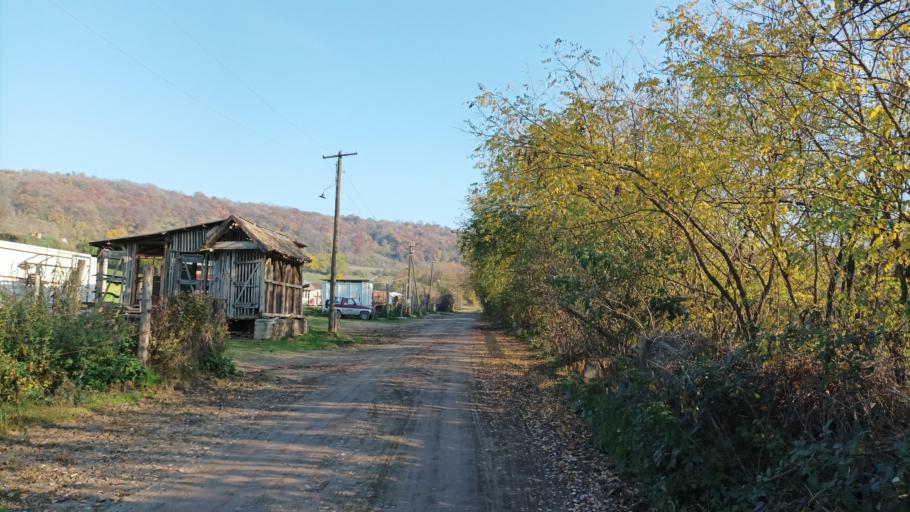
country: HU
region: Tolna
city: Szentgalpuszta
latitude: 46.3401
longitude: 18.6014
